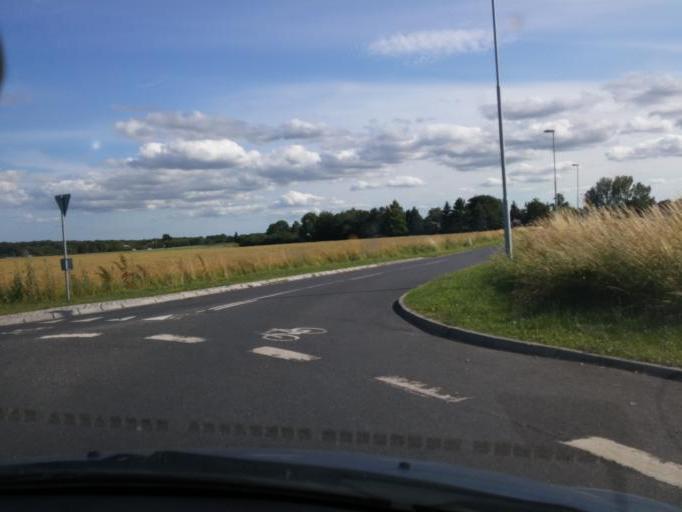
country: DK
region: South Denmark
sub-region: Kerteminde Kommune
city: Munkebo
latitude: 55.4376
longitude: 10.5408
